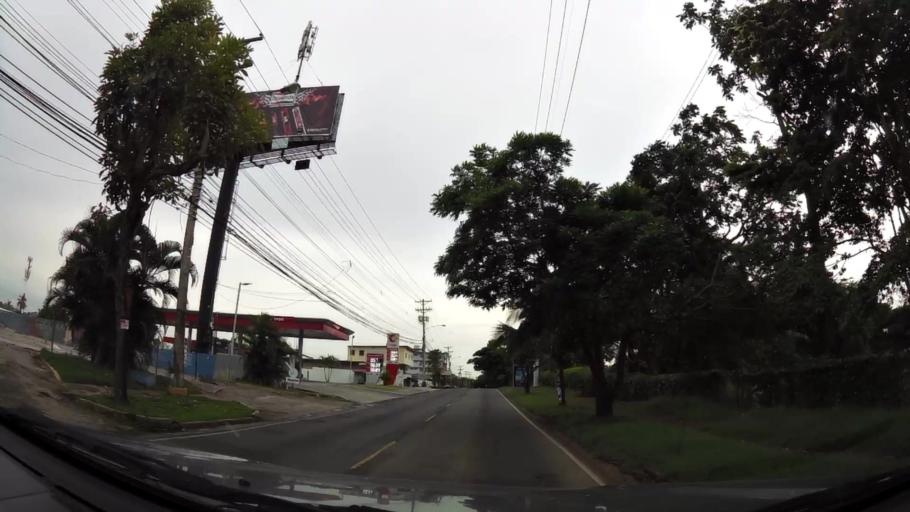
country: PA
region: Panama
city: Panama
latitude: 9.0129
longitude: -79.4923
